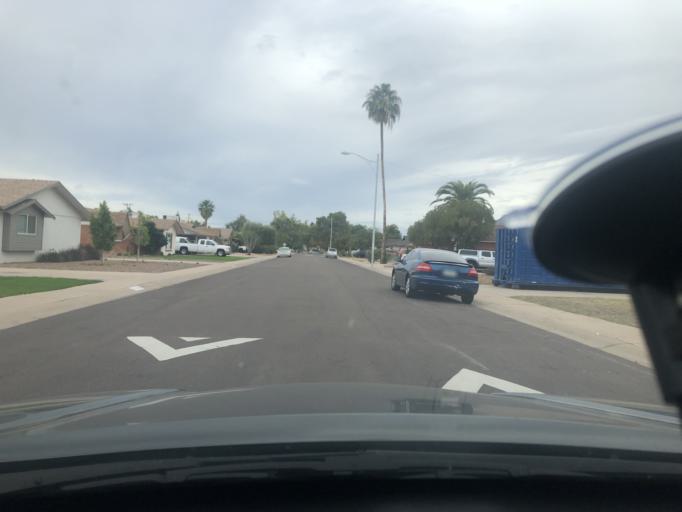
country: US
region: Arizona
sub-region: Maricopa County
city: Scottsdale
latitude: 33.4971
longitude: -111.9023
